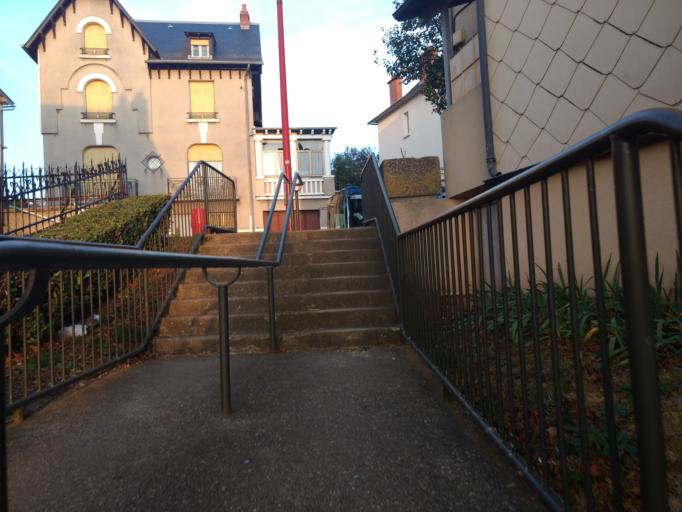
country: FR
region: Midi-Pyrenees
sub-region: Departement de l'Aveyron
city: Rodez
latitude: 44.3597
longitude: 2.5801
